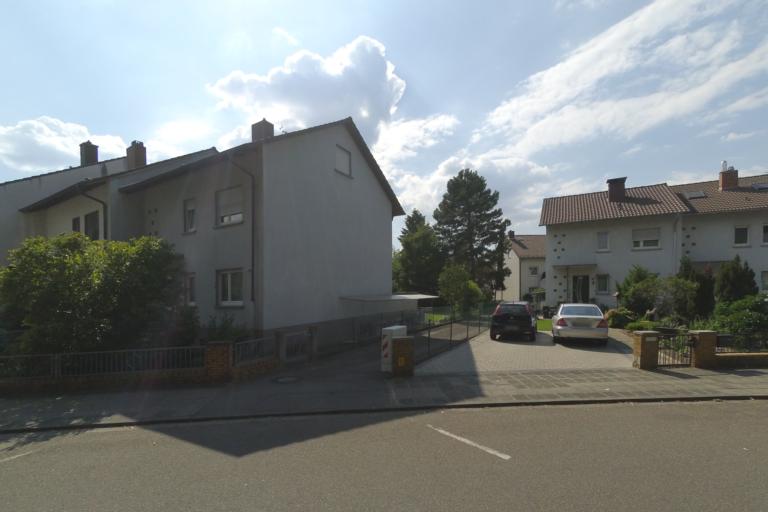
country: DE
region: Hesse
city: Viernheim
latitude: 49.5327
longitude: 8.5621
